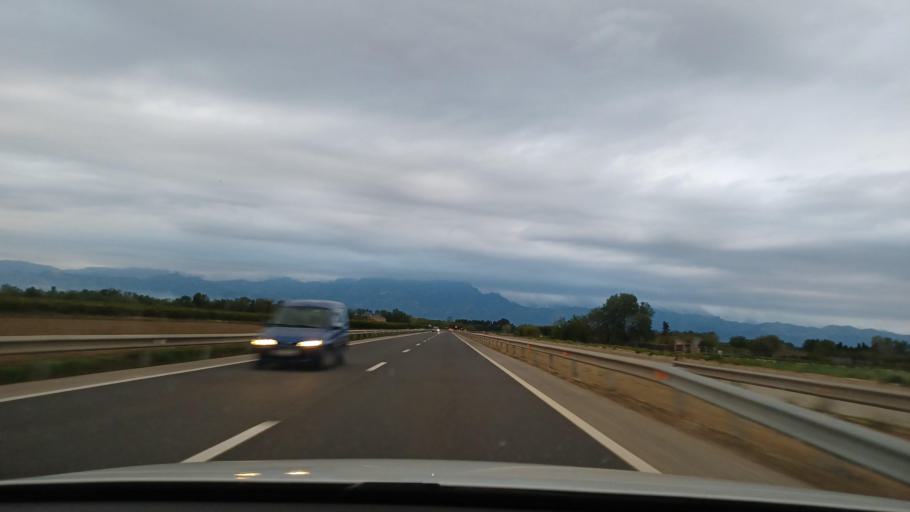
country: ES
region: Catalonia
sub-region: Provincia de Tarragona
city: Masdenverge
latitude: 40.7500
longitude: 0.5502
